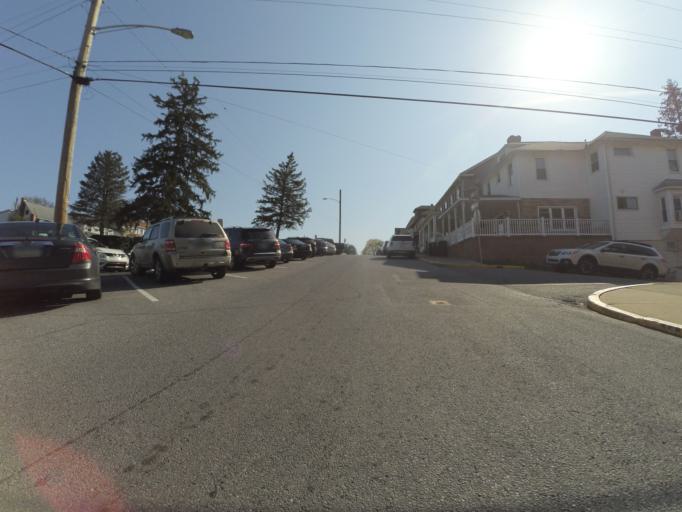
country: US
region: Pennsylvania
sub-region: Centre County
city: Bellefonte
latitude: 40.9122
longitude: -77.7765
